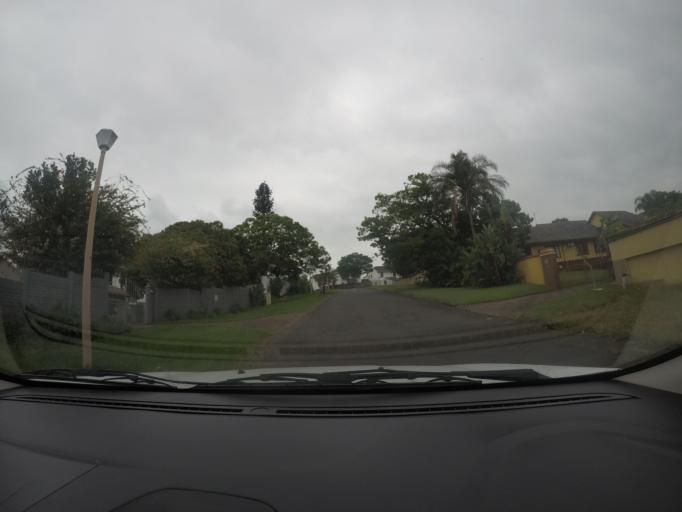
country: ZA
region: KwaZulu-Natal
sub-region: uThungulu District Municipality
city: Empangeni
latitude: -28.7587
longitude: 31.8887
